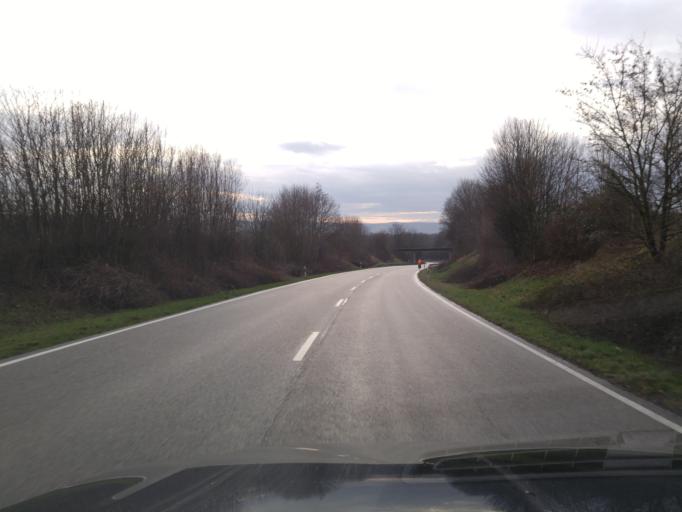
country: DE
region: Baden-Wuerttemberg
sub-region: Regierungsbezirk Stuttgart
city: Neuenstein
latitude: 49.2077
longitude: 9.5973
